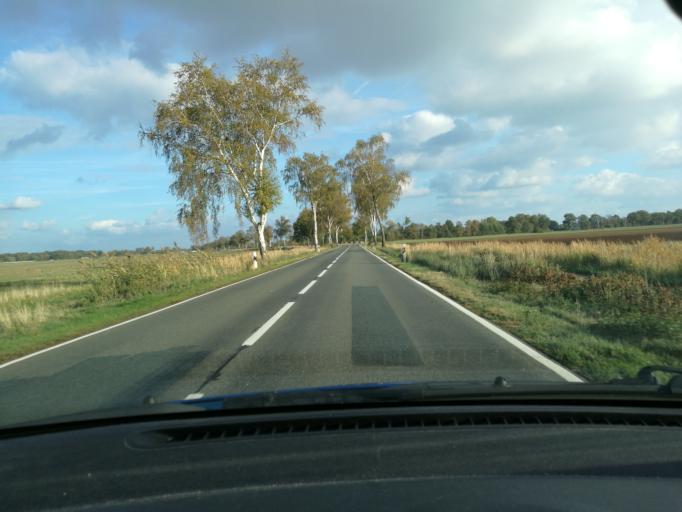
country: DE
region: Lower Saxony
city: Prezelle
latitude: 52.9074
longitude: 11.3869
